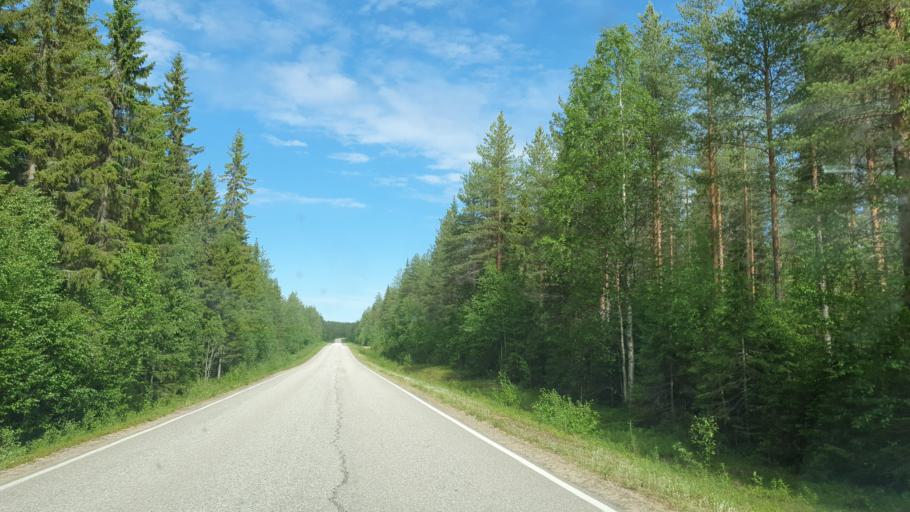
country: FI
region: Kainuu
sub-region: Kehys-Kainuu
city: Suomussalmi
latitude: 64.5890
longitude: 29.0723
